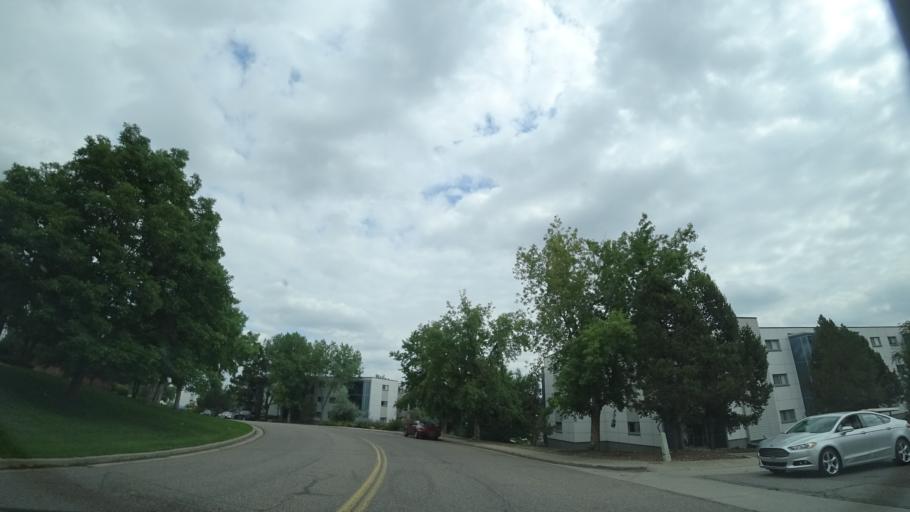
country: US
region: Colorado
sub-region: Jefferson County
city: West Pleasant View
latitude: 39.7169
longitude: -105.1635
